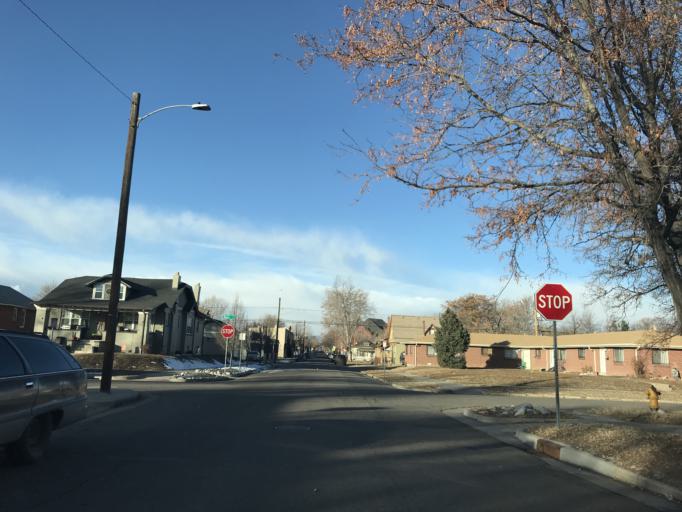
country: US
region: Colorado
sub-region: Denver County
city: Denver
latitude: 39.7670
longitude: -104.9632
